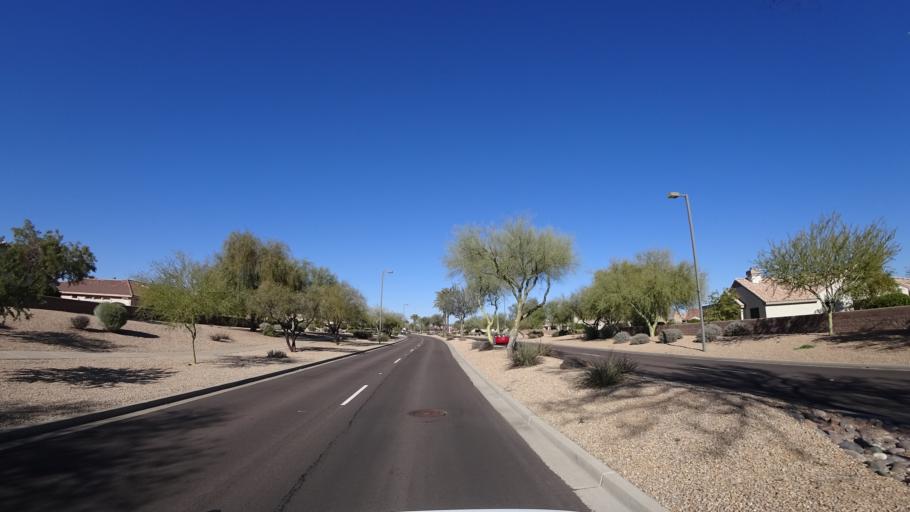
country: US
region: Arizona
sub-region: Maricopa County
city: Sun City West
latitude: 33.6484
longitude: -112.4065
